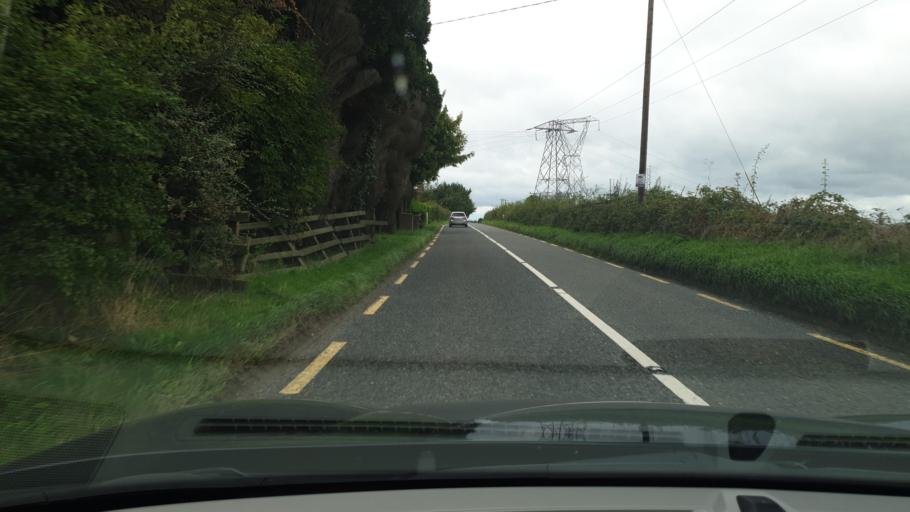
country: IE
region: Leinster
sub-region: Kildare
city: Naas
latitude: 53.2225
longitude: -6.7036
